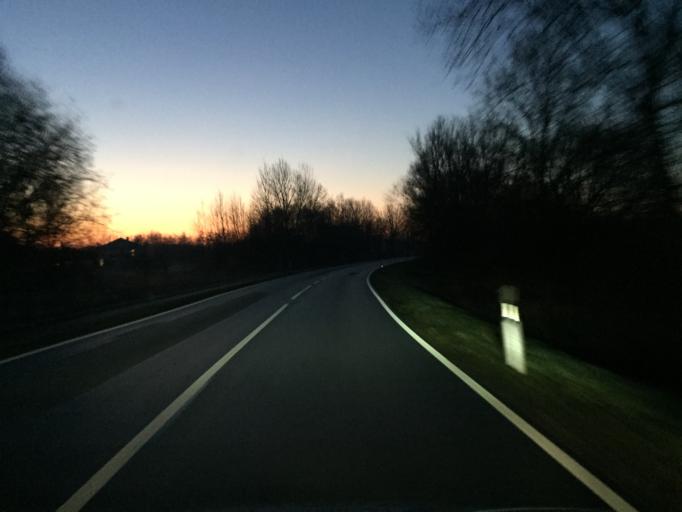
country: DE
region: Lower Saxony
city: Steyerberg
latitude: 52.5700
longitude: 9.0102
